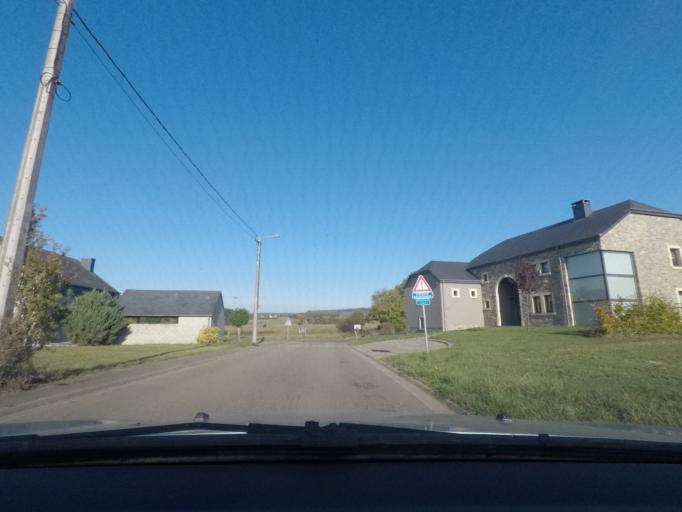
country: BE
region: Wallonia
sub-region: Province du Luxembourg
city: Arlon
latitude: 49.6390
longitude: 5.7944
